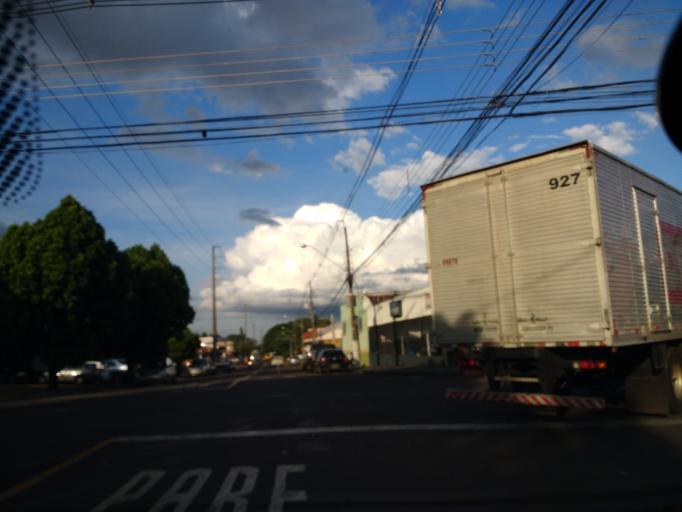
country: BR
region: Parana
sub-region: Londrina
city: Londrina
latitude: -23.2957
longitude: -51.1629
